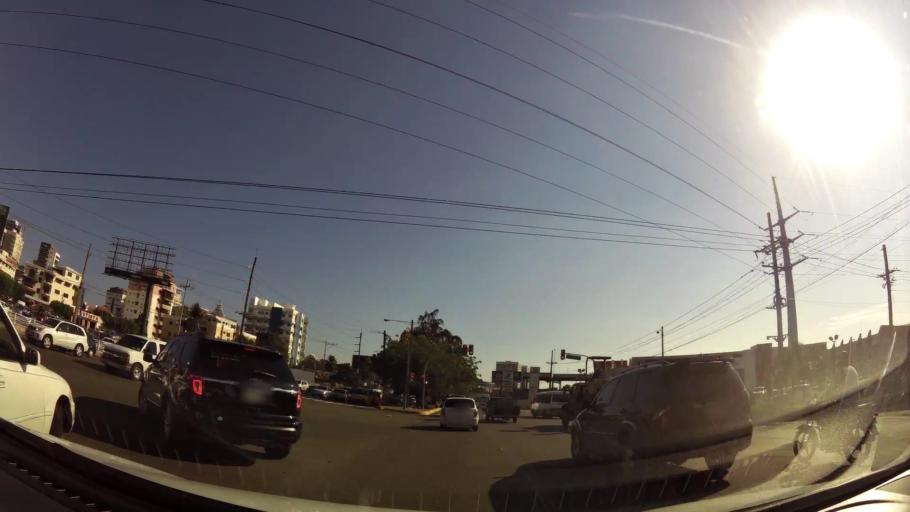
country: DO
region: Nacional
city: Bella Vista
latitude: 18.4445
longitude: -69.9770
